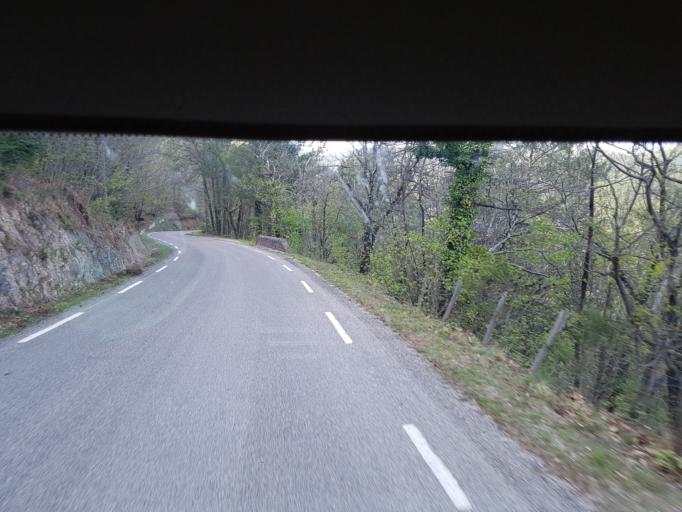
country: FR
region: Languedoc-Roussillon
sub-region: Departement du Gard
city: Branoux-les-Taillades
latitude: 44.3359
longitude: 3.9543
